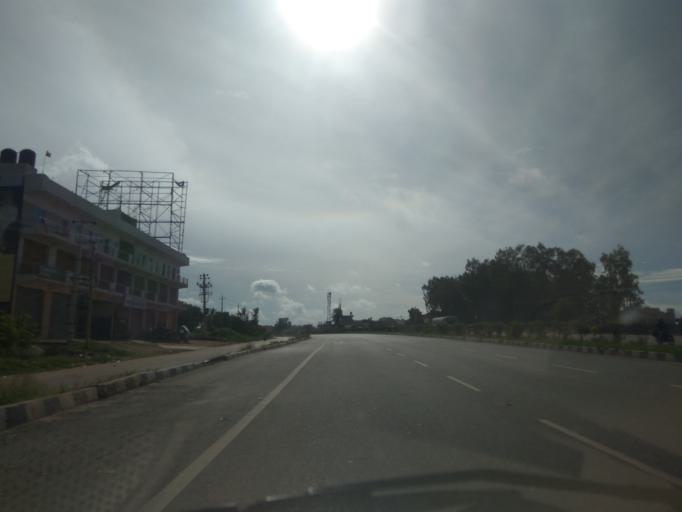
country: IN
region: Karnataka
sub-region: Bangalore Rural
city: Hoskote
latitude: 13.0771
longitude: 77.8049
